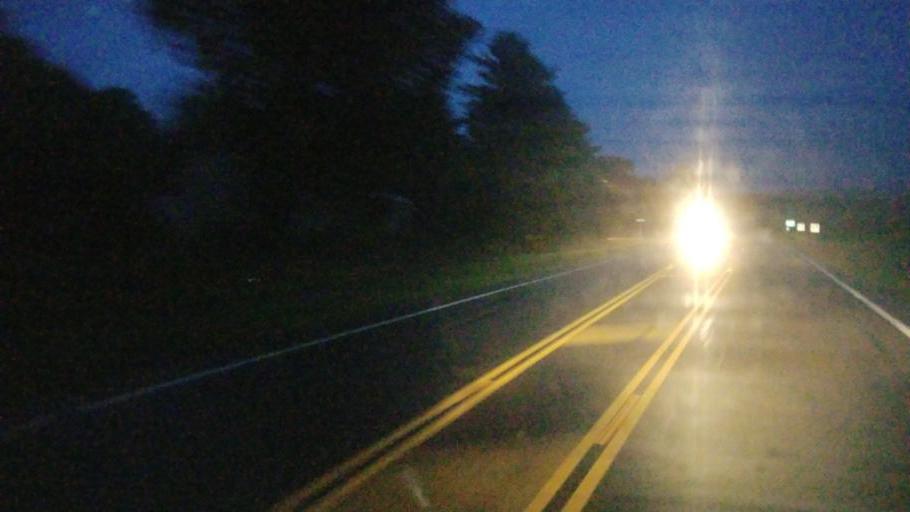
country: US
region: Ohio
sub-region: Knox County
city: Gambier
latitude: 40.3672
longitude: -82.3951
